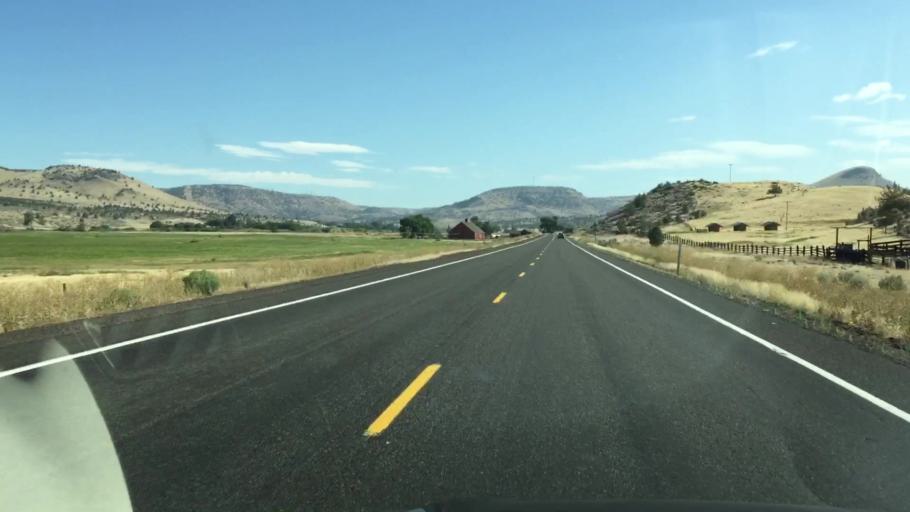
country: US
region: Oregon
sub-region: Jefferson County
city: Madras
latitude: 44.7928
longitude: -120.9510
